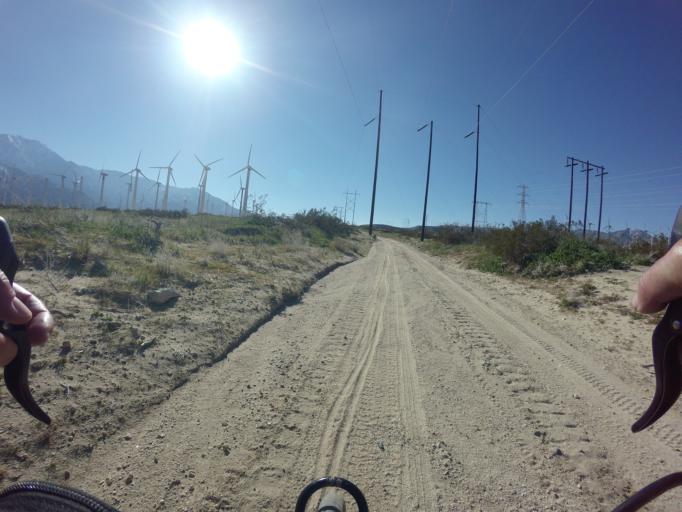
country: US
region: California
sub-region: Riverside County
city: Garnet
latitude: 33.9322
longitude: -116.6227
